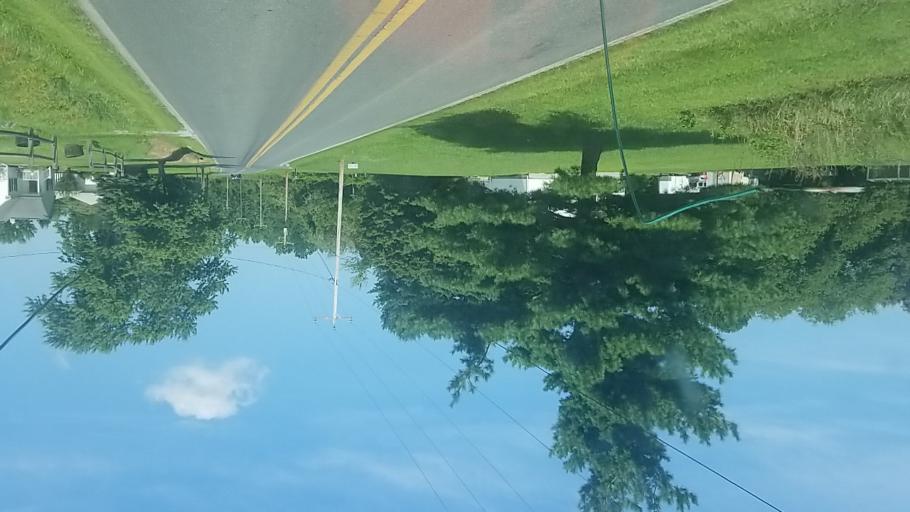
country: US
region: Maryland
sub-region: Caroline County
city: Denton
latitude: 38.8798
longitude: -75.7963
